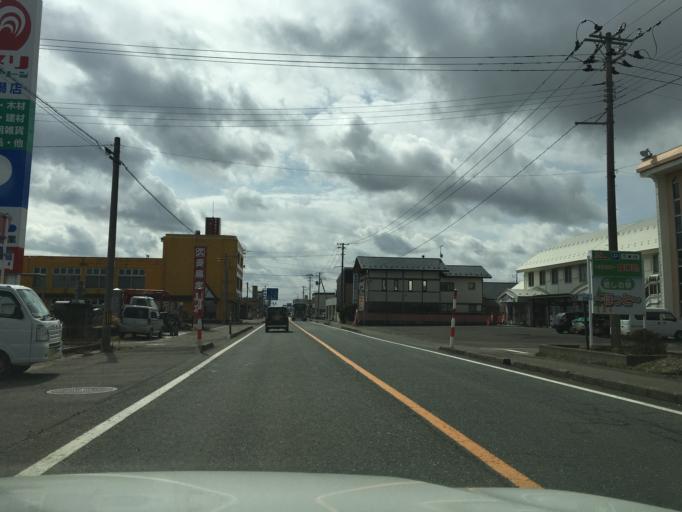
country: JP
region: Akita
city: Tenno
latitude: 39.9467
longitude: 140.0836
